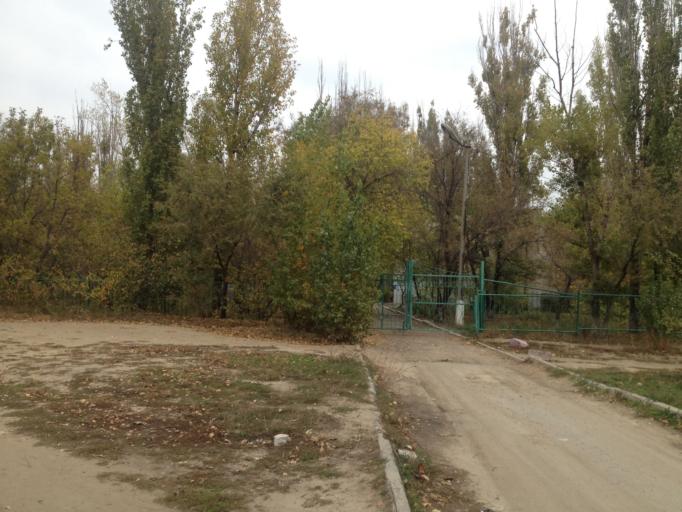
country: RU
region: Volgograd
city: Volgograd
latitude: 48.7379
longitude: 44.4874
